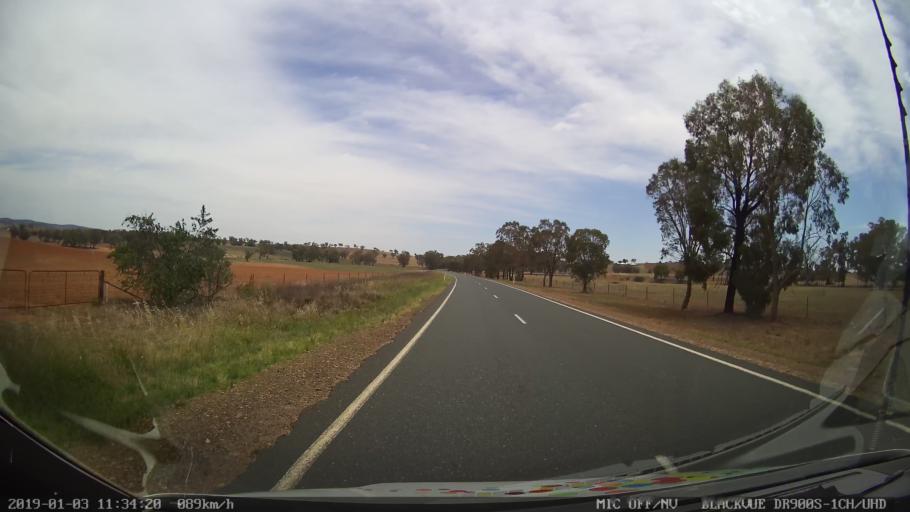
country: AU
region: New South Wales
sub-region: Weddin
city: Grenfell
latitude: -33.9361
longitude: 148.1645
